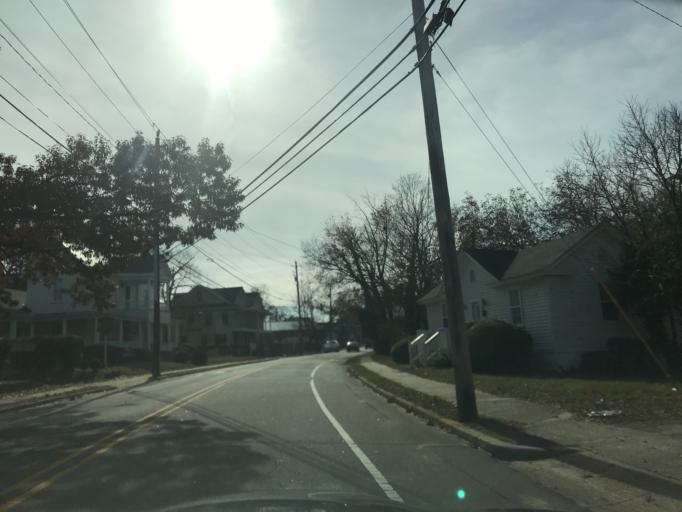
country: US
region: North Carolina
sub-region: Wake County
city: West Raleigh
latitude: 35.7967
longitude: -78.6604
